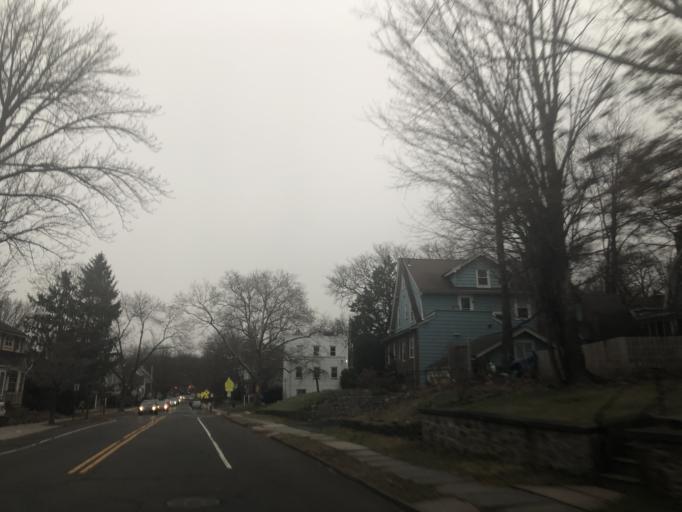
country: US
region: New Jersey
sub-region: Essex County
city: South Orange
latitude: 40.7420
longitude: -74.2579
